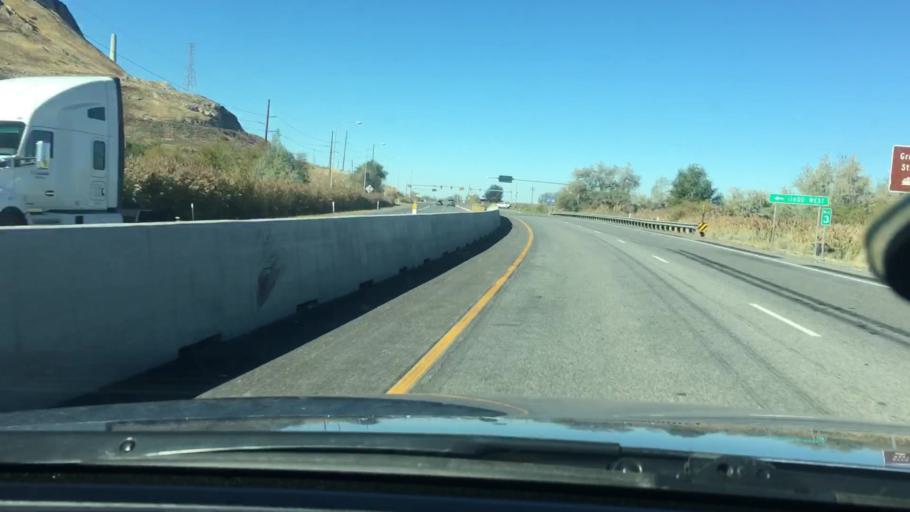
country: US
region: Utah
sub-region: Salt Lake County
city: Magna
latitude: 40.7276
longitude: -112.1669
